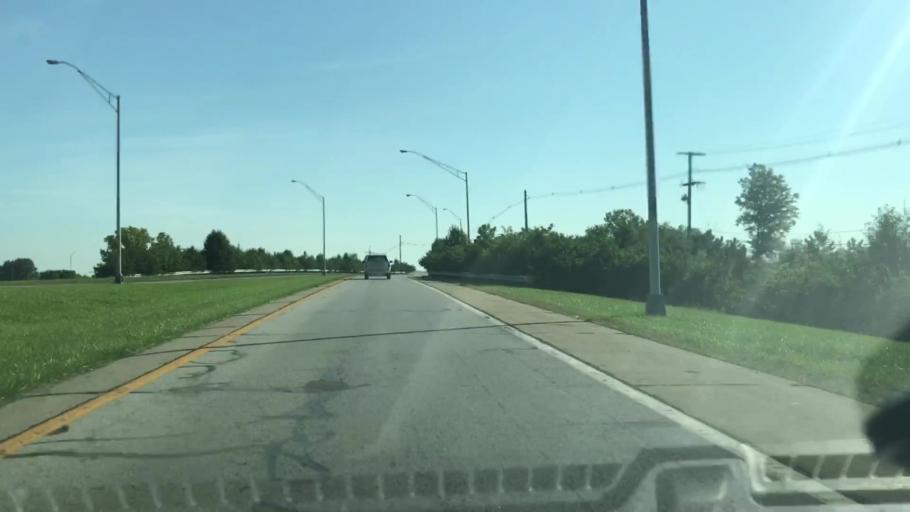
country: US
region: Ohio
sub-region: Franklin County
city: Bexley
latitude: 39.9995
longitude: -82.9249
